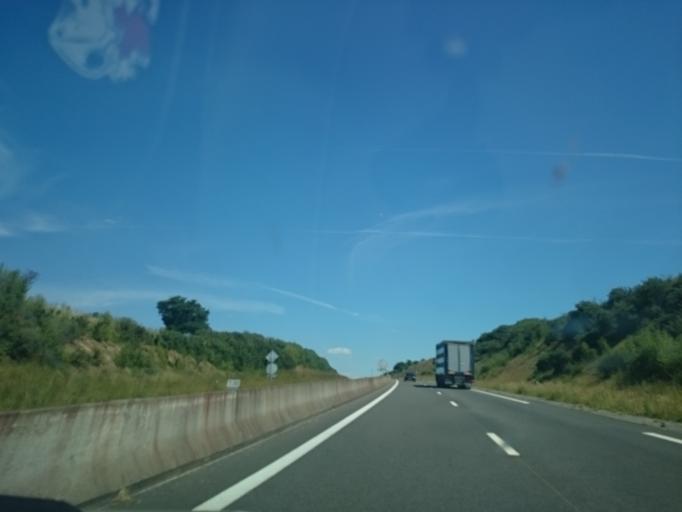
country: FR
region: Brittany
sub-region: Departement des Cotes-d'Armor
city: Gouarec
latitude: 48.2233
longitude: -3.1036
